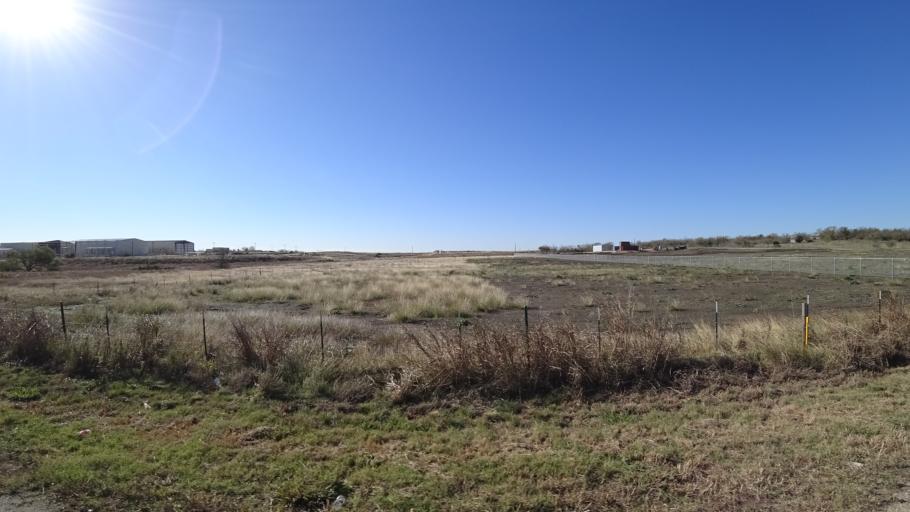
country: US
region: Texas
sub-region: Travis County
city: Onion Creek
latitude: 30.1229
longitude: -97.6701
